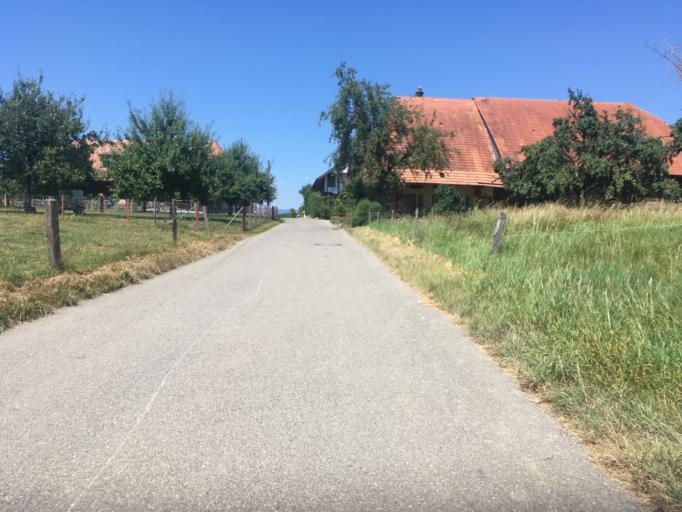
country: CH
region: Solothurn
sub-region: Bezirk Bucheggberg
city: Messen
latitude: 47.0758
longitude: 7.4173
